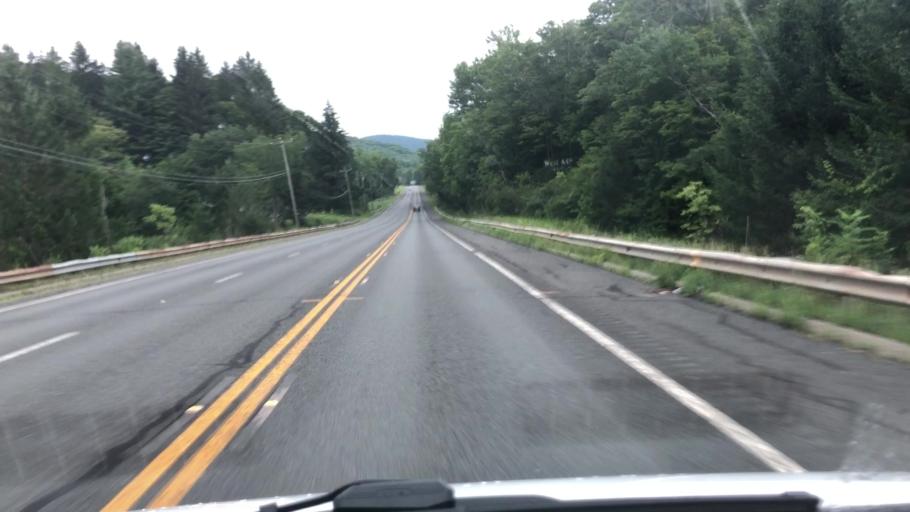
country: US
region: Massachusetts
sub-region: Berkshire County
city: Lanesborough
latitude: 42.5968
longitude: -73.2431
